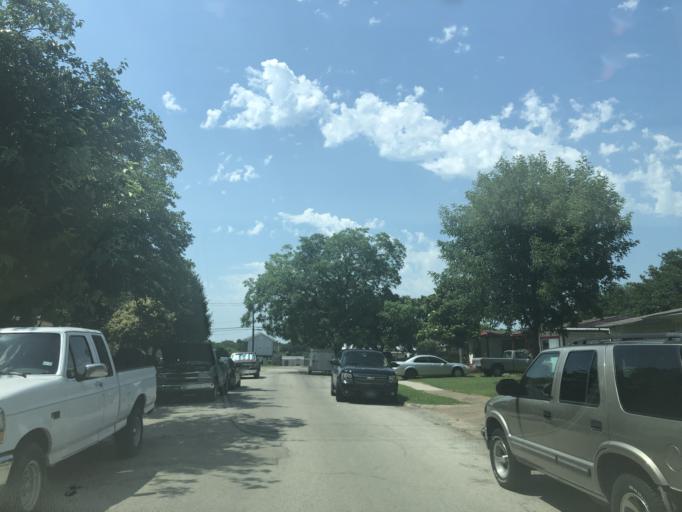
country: US
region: Texas
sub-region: Dallas County
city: Grand Prairie
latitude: 32.7295
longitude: -97.0131
